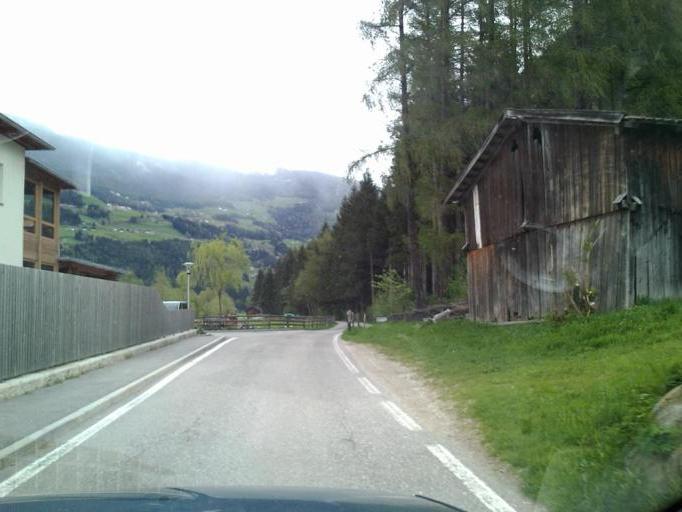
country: IT
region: Trentino-Alto Adige
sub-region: Bolzano
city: Campo Tures
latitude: 46.9046
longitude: 11.9587
